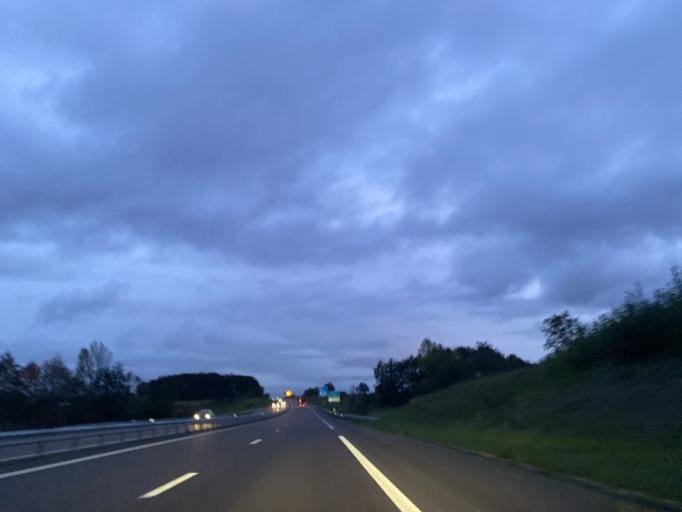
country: FR
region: Auvergne
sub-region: Departement de l'Allier
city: Estivareilles
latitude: 46.4192
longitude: 2.7026
